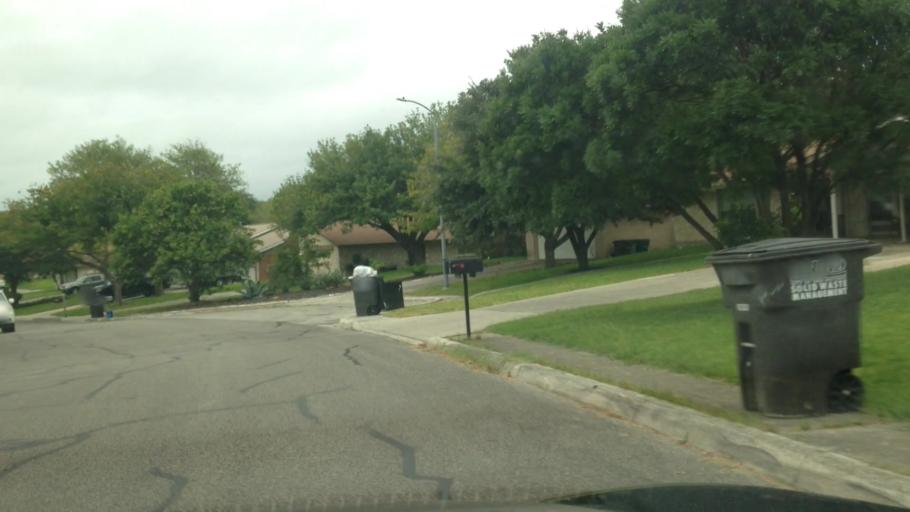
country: US
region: Texas
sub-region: Bexar County
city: Windcrest
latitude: 29.5733
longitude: -98.4140
